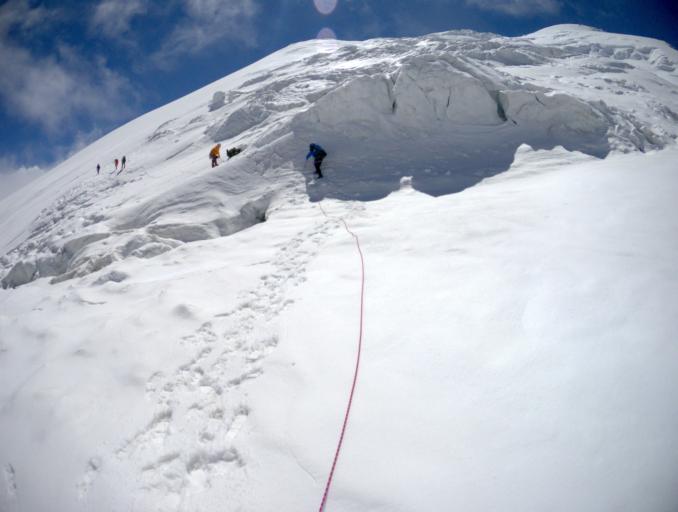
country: RU
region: Kabardino-Balkariya
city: Terskol
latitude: 43.3797
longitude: 42.4536
